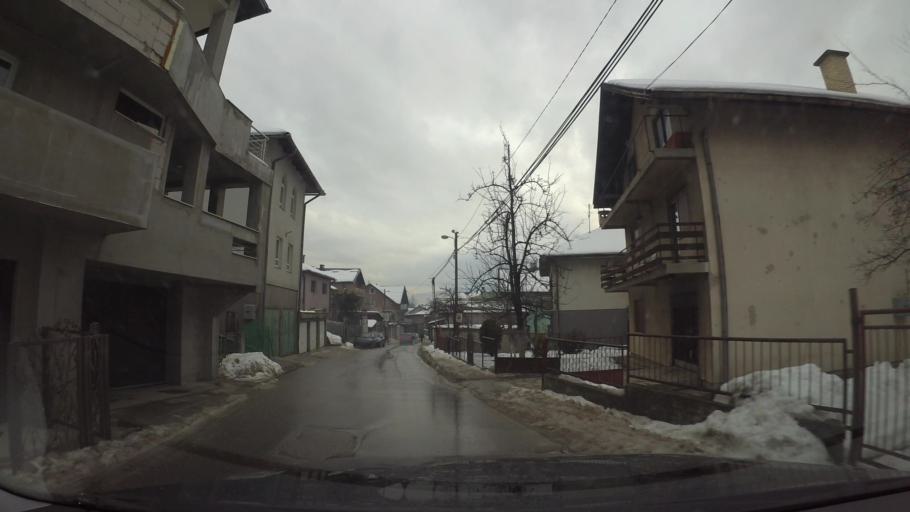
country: BA
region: Federation of Bosnia and Herzegovina
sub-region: Kanton Sarajevo
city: Sarajevo
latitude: 43.8572
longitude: 18.3458
